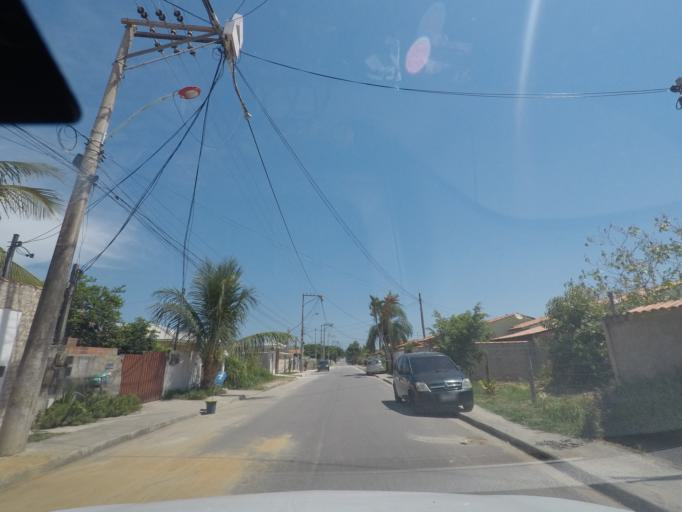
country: BR
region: Rio de Janeiro
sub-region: Marica
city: Marica
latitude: -22.9612
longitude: -42.9567
